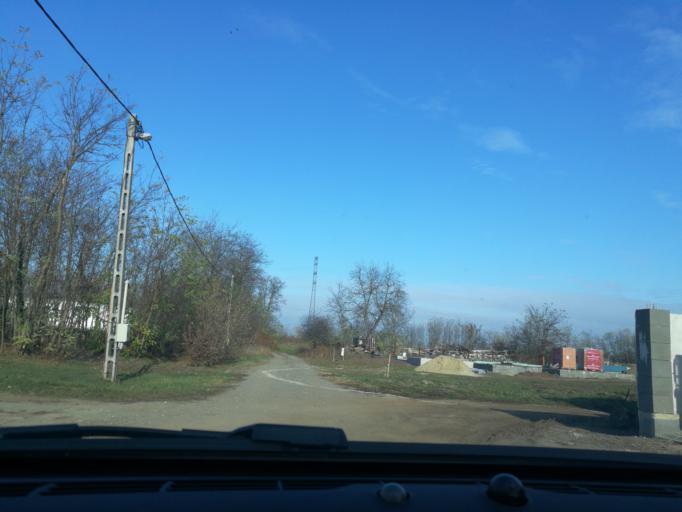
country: HU
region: Szabolcs-Szatmar-Bereg
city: Nyiregyhaza
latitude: 47.9589
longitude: 21.7560
